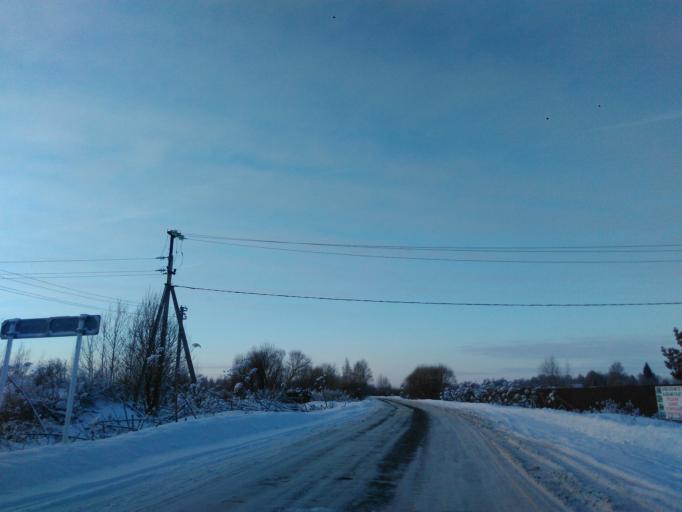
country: RU
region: Tverskaya
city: Zavidovo
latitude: 56.6309
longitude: 36.6184
